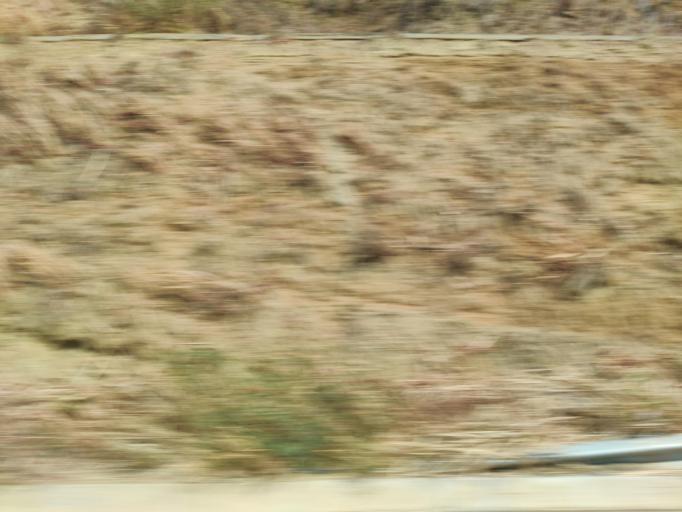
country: CO
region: Atlantico
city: Puerto Colombia
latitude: 10.9424
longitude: -75.0131
